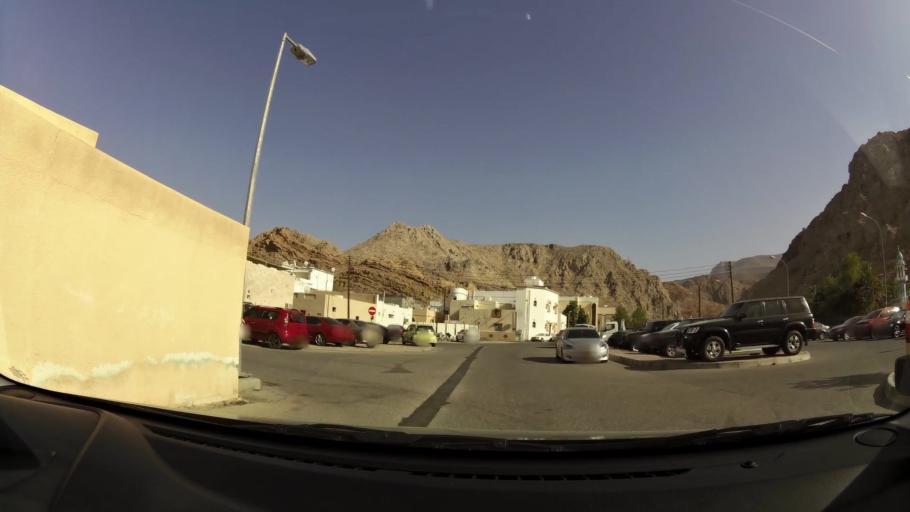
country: OM
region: Muhafazat Masqat
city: Muscat
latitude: 23.5848
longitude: 58.5158
